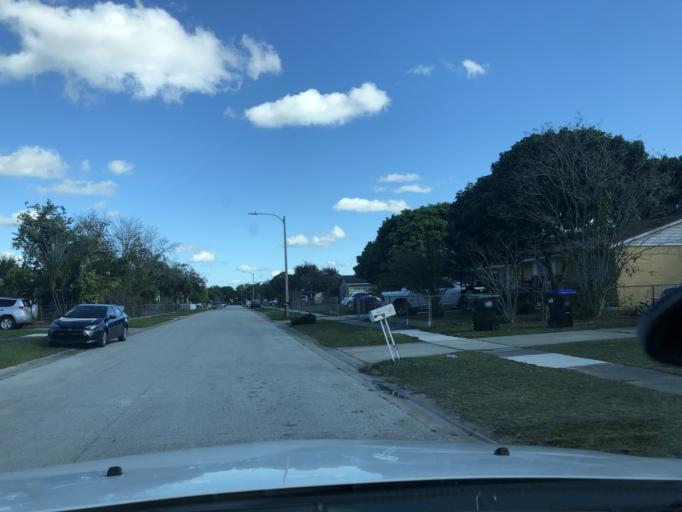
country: US
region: Florida
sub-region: Orange County
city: Oak Ridge
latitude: 28.4783
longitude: -81.4365
